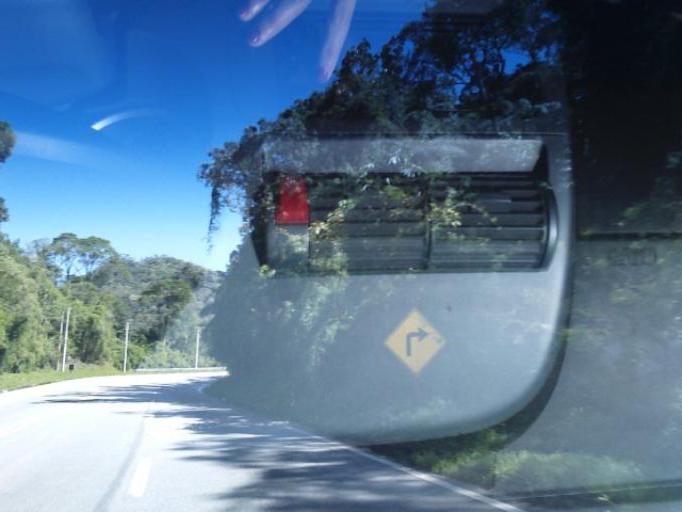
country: BR
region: Sao Paulo
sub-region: Campos Do Jordao
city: Campos do Jordao
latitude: -22.8207
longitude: -45.6239
